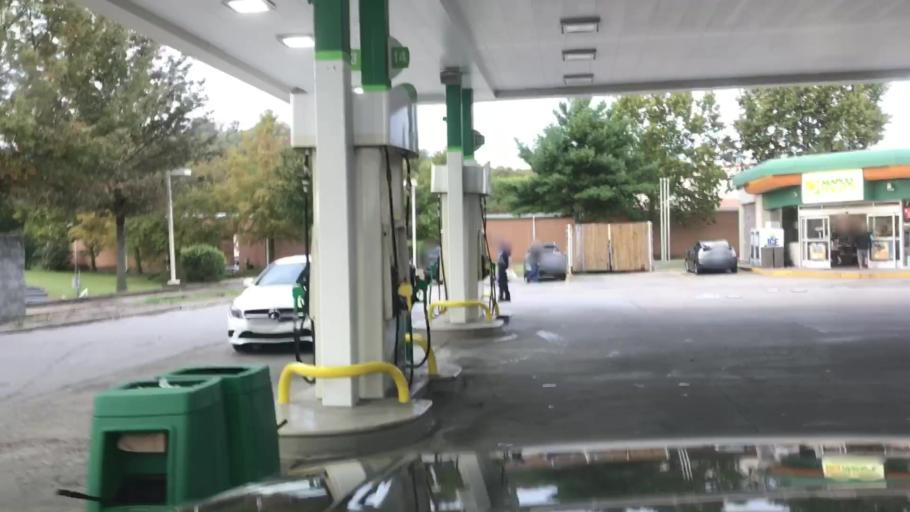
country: US
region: Tennessee
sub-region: Williamson County
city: Brentwood Estates
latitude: 35.9676
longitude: -86.8141
